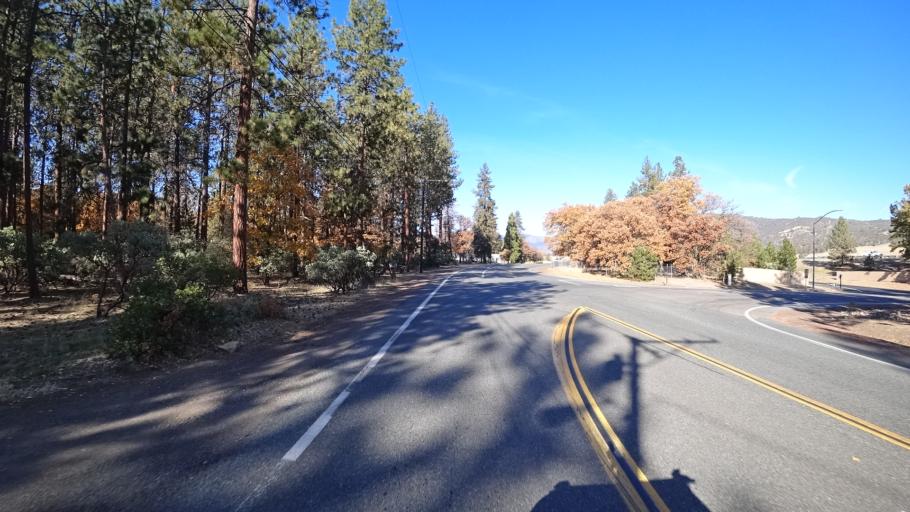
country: US
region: California
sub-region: Siskiyou County
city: Yreka
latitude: 41.6670
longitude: -122.6111
